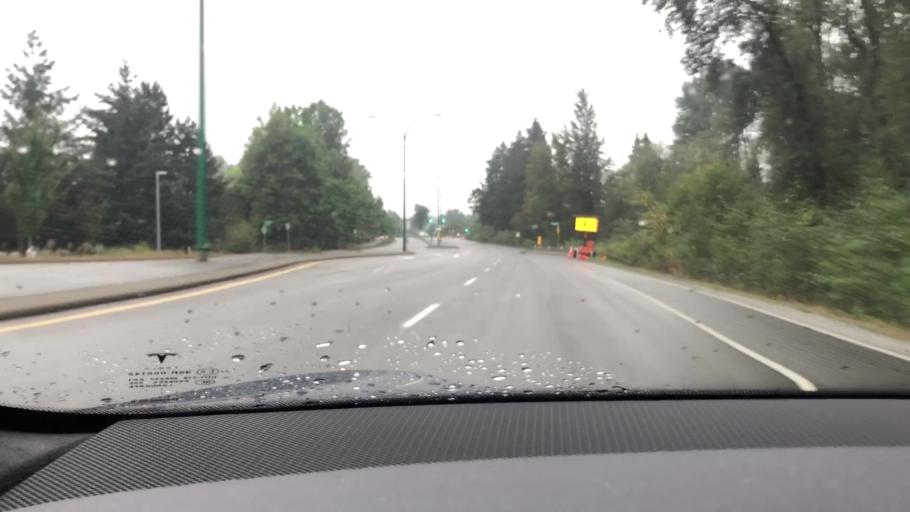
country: CA
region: British Columbia
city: Burnaby
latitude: 49.2472
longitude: -122.9666
